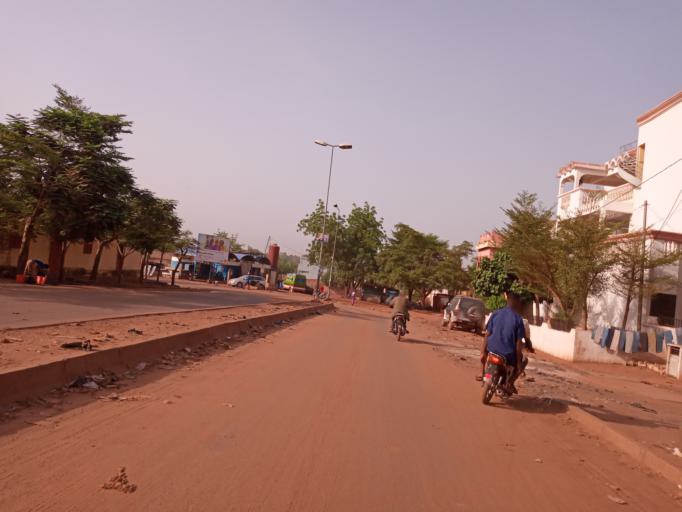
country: ML
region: Bamako
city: Bamako
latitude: 12.6632
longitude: -7.9790
